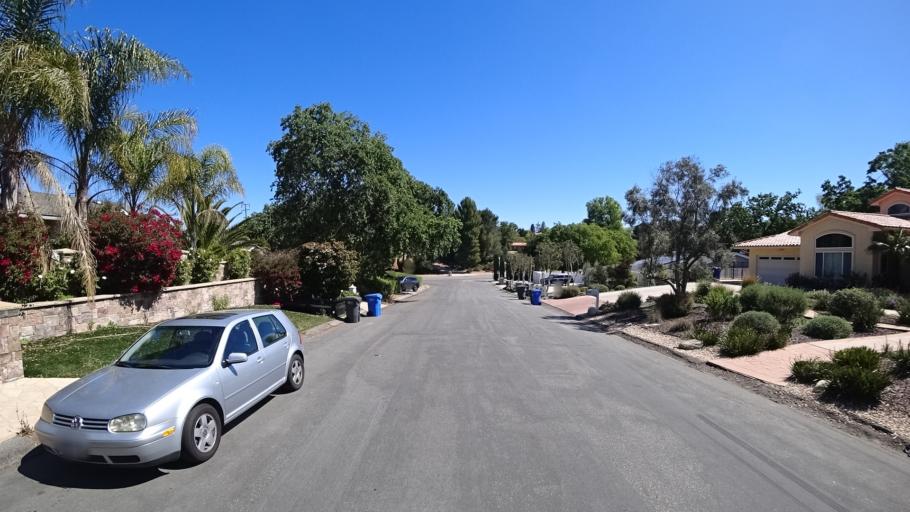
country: US
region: California
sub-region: Ventura County
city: Thousand Oaks
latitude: 34.1912
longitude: -118.8592
